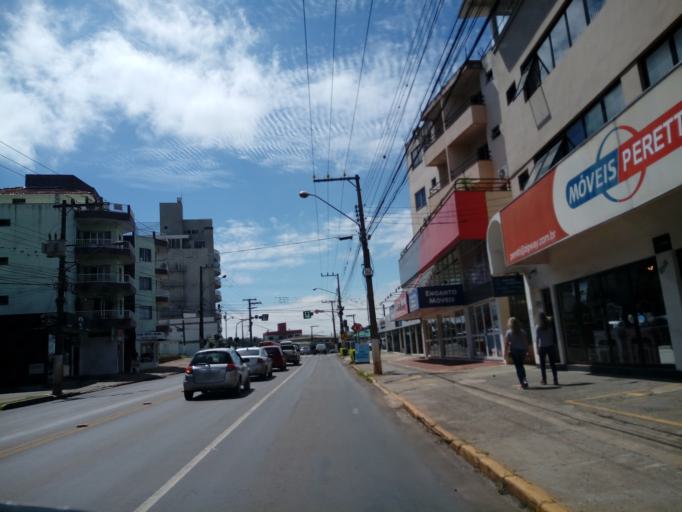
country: BR
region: Santa Catarina
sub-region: Chapeco
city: Chapeco
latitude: -27.0944
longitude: -52.6263
